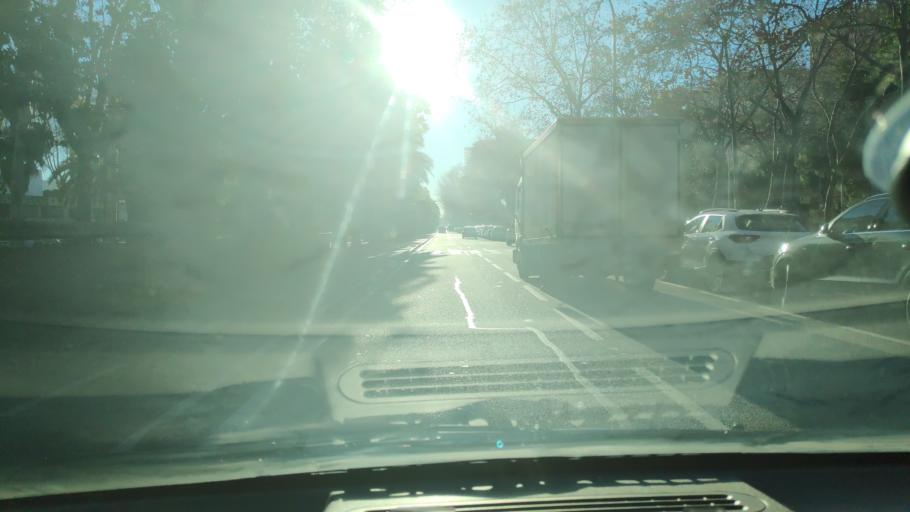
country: ES
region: Catalonia
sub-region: Provincia de Barcelona
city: Sant Marti
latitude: 41.4154
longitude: 2.2136
